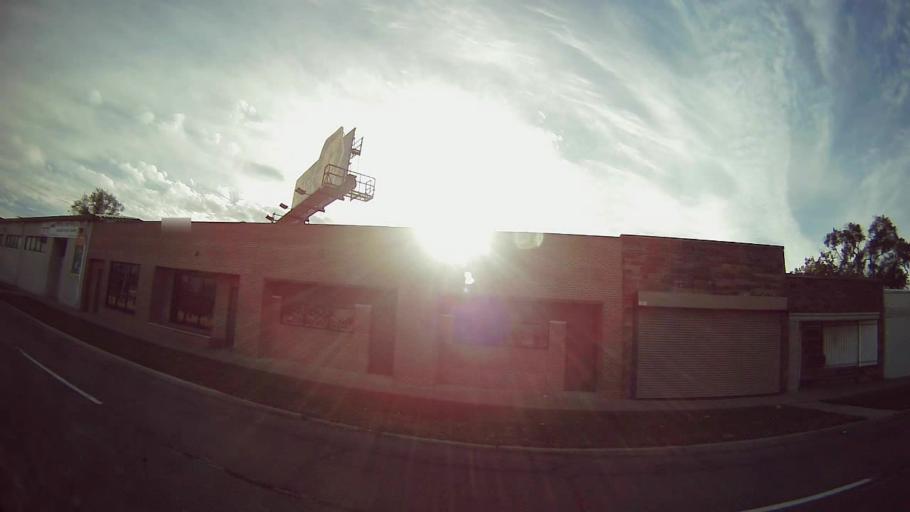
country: US
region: Michigan
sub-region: Oakland County
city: Oak Park
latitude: 42.4160
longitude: -83.1717
